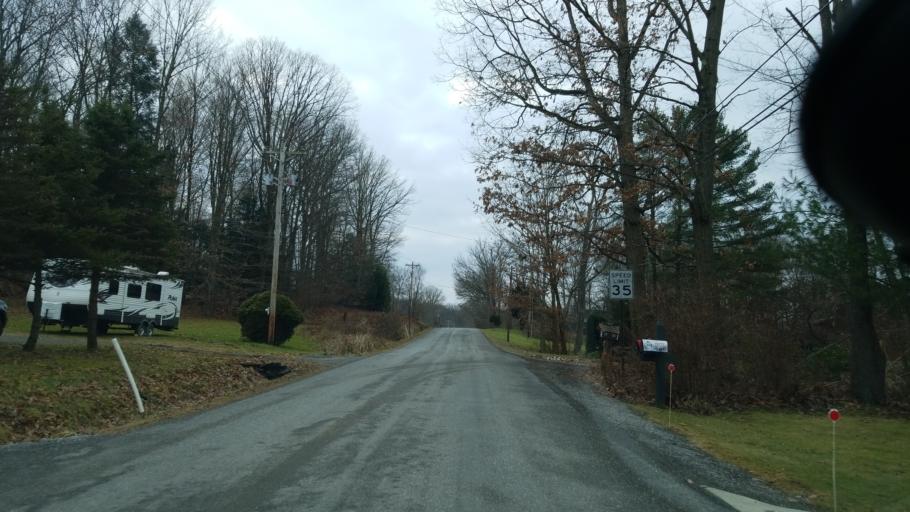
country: US
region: Pennsylvania
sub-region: Clearfield County
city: Treasure Lake
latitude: 41.1122
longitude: -78.6927
